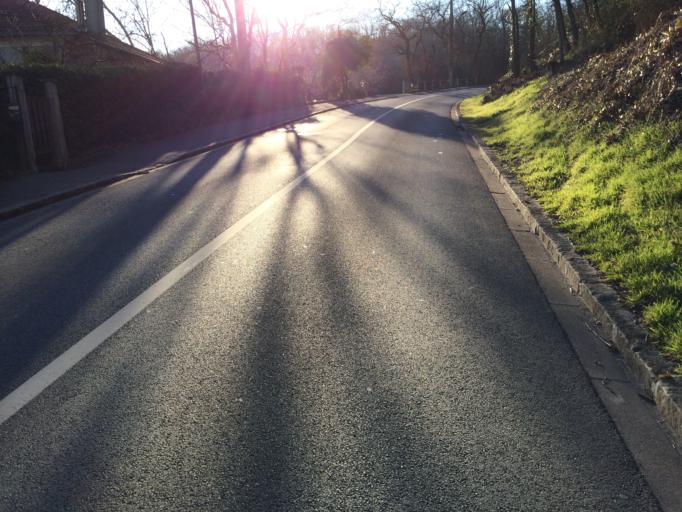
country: FR
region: Ile-de-France
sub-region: Departement de l'Essonne
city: Villebon-sur-Yvette
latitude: 48.7151
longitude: 2.2402
